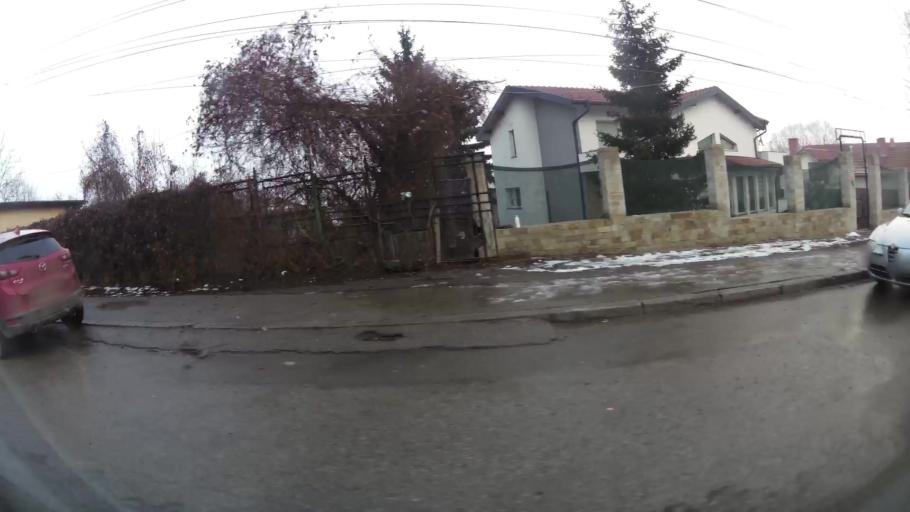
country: BG
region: Sofia-Capital
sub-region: Stolichna Obshtina
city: Sofia
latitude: 42.6496
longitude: 23.2624
